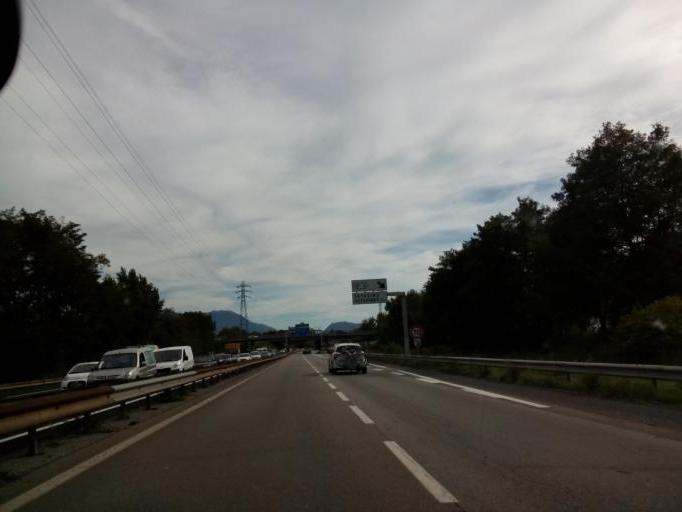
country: FR
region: Rhone-Alpes
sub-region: Departement de l'Isere
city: Grenoble
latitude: 45.1614
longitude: 5.7014
